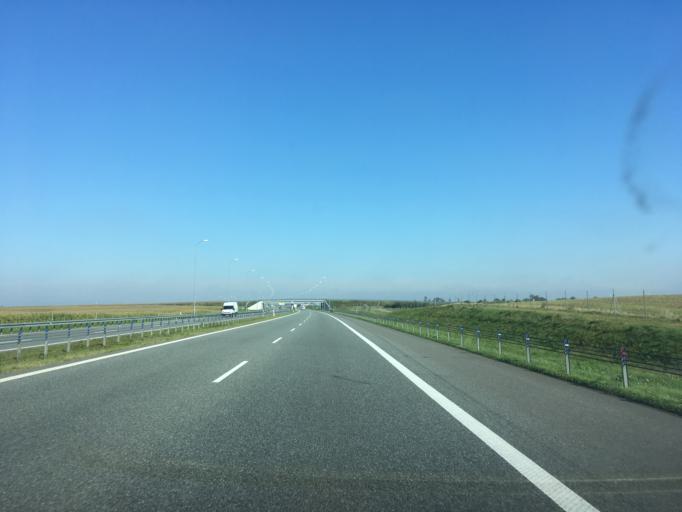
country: PL
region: Kujawsko-Pomorskie
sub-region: Powiat chelminski
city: Lisewo
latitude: 53.2511
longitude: 18.7260
